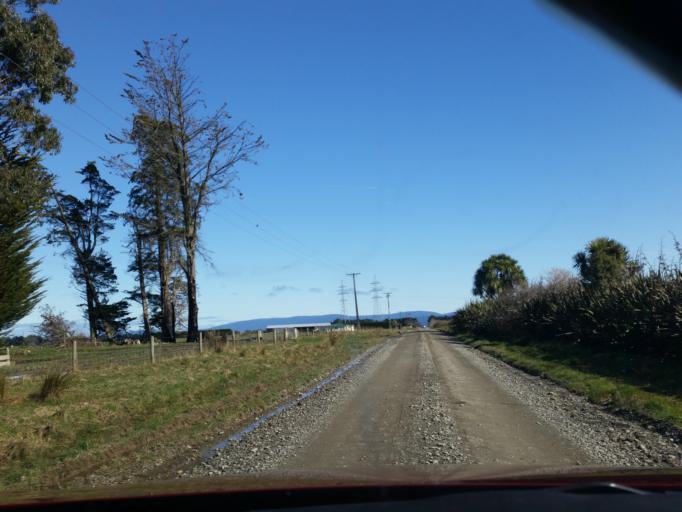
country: NZ
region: Southland
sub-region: Southland District
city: Winton
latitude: -46.2055
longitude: 168.2103
